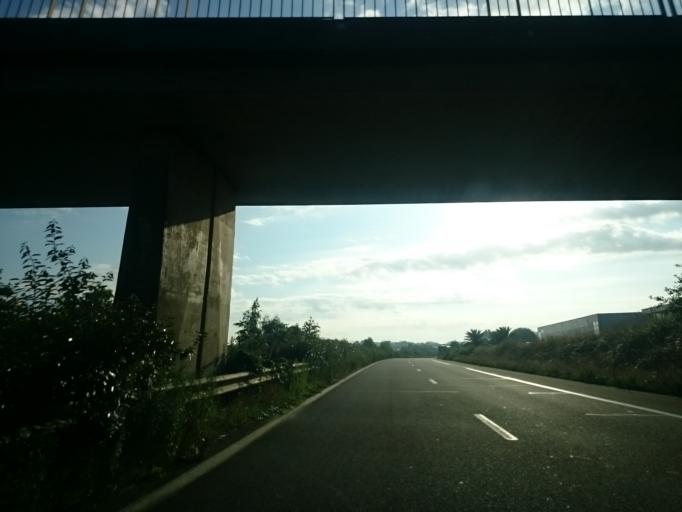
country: FR
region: Brittany
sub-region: Departement du Finistere
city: Landivisiau
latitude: 48.5173
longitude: -4.0816
